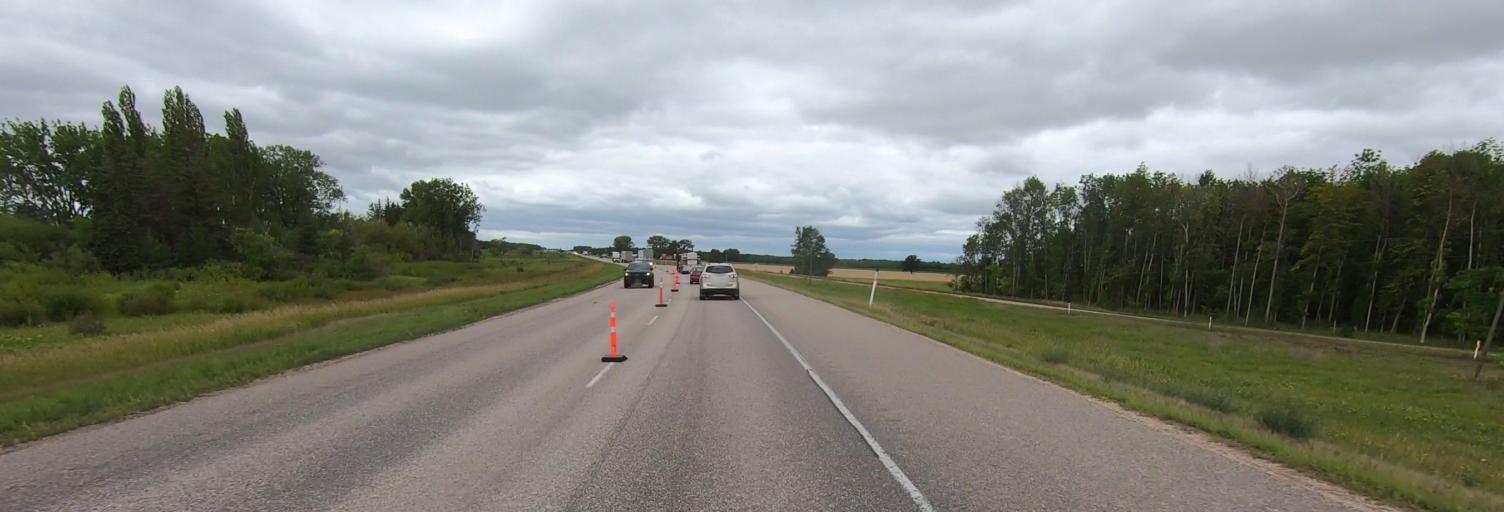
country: CA
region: Manitoba
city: Portage la Prairie
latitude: 49.9723
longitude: -98.1027
